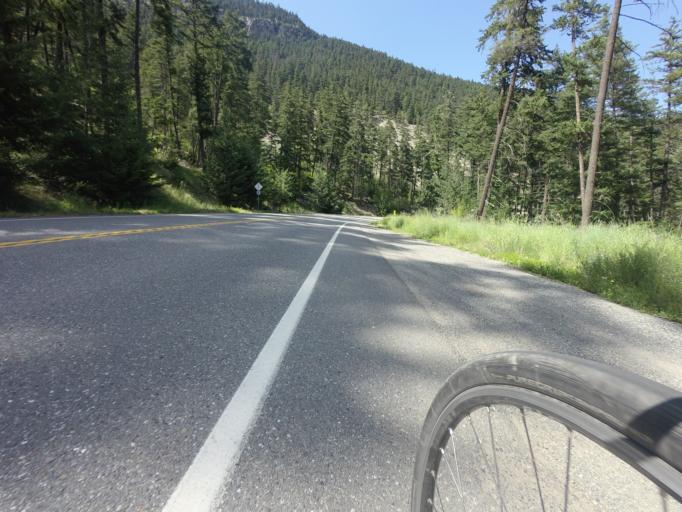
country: CA
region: British Columbia
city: Lillooet
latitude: 50.6530
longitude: -122.0105
